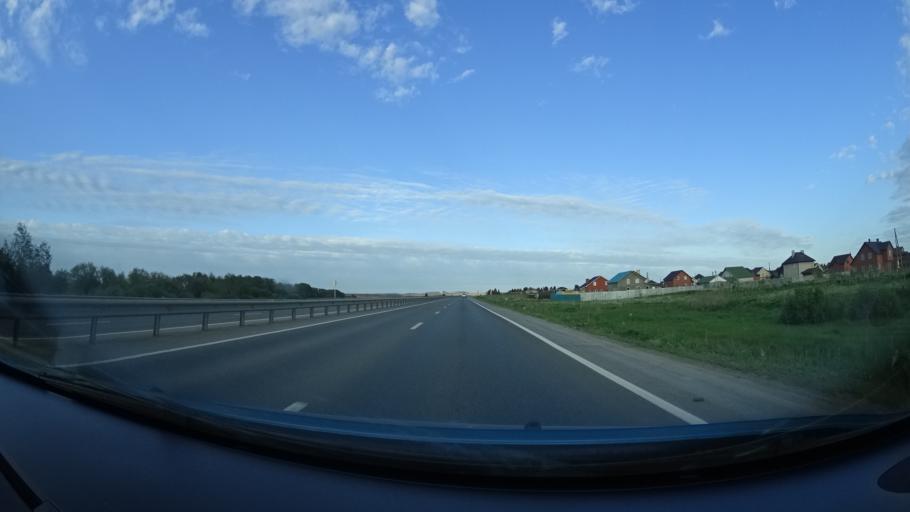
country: RU
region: Perm
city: Kultayevo
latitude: 57.9008
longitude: 55.9742
